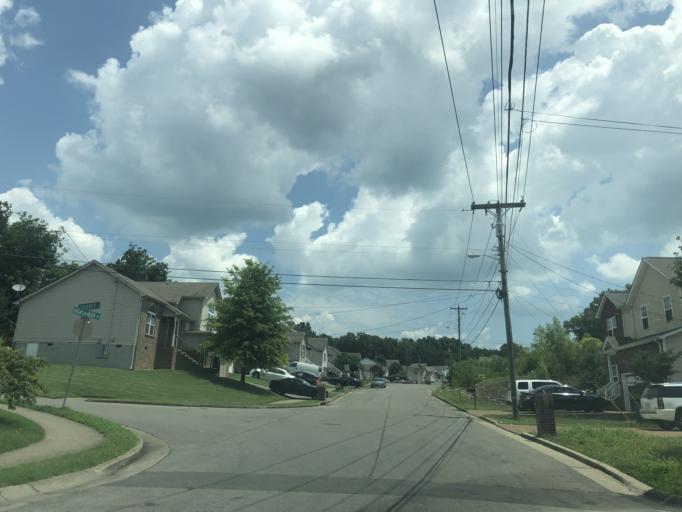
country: US
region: Tennessee
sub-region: Rutherford County
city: La Vergne
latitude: 36.0584
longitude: -86.6559
